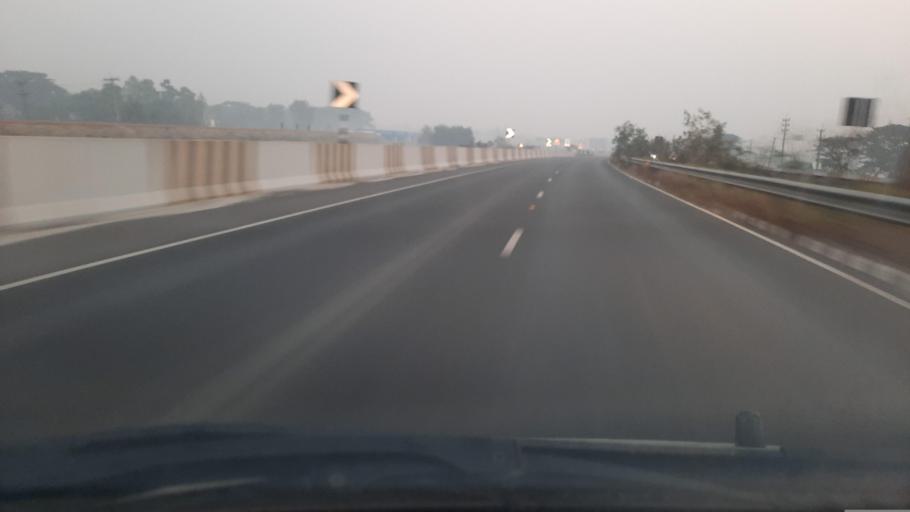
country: BD
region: Dhaka
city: Dohar
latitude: 23.5258
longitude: 90.2862
